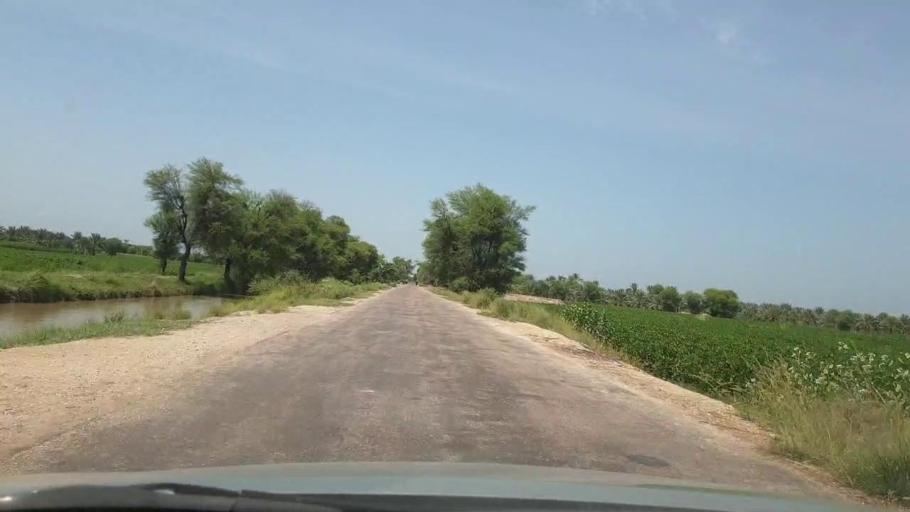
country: PK
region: Sindh
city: Pano Aqil
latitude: 27.6778
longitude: 69.1094
